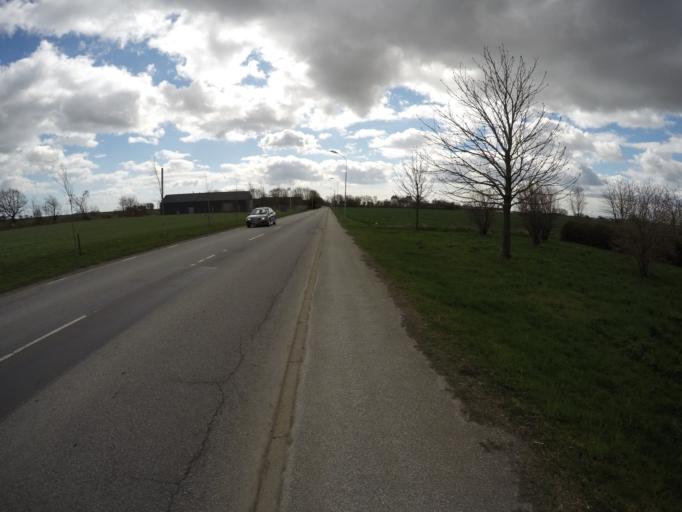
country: SE
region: Skane
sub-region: Ystads Kommun
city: Kopingebro
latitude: 55.4327
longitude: 14.1133
